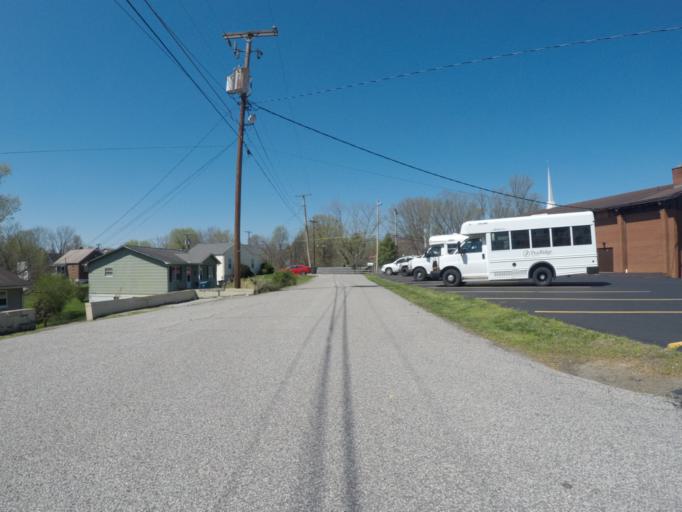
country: US
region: West Virginia
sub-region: Cabell County
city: Pea Ridge
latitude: 38.4147
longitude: -82.3189
